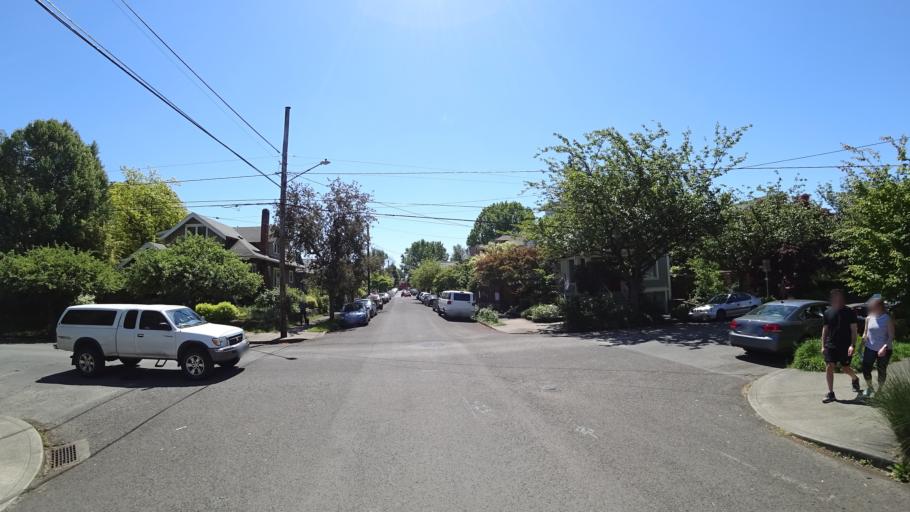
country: US
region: Oregon
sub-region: Multnomah County
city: Portland
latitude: 45.5144
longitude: -122.6269
